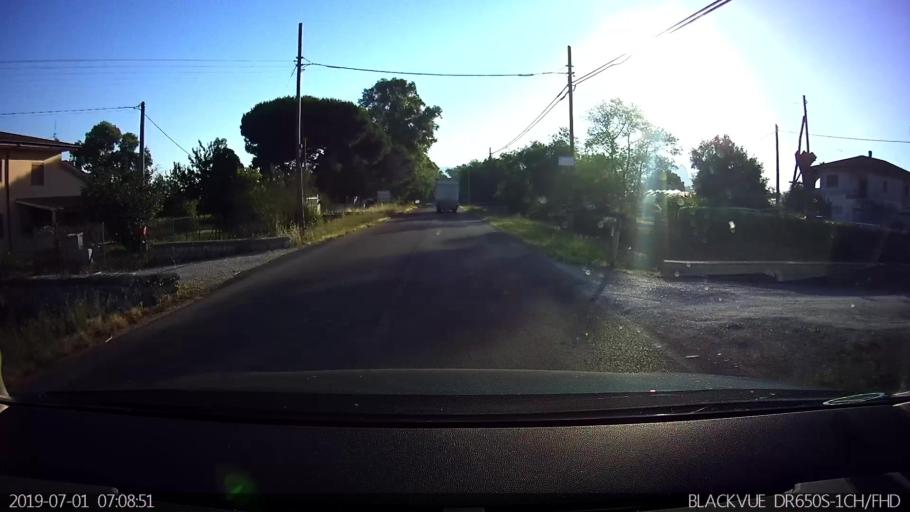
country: IT
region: Latium
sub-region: Provincia di Latina
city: Borgo Hermada
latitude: 41.3008
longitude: 13.1548
